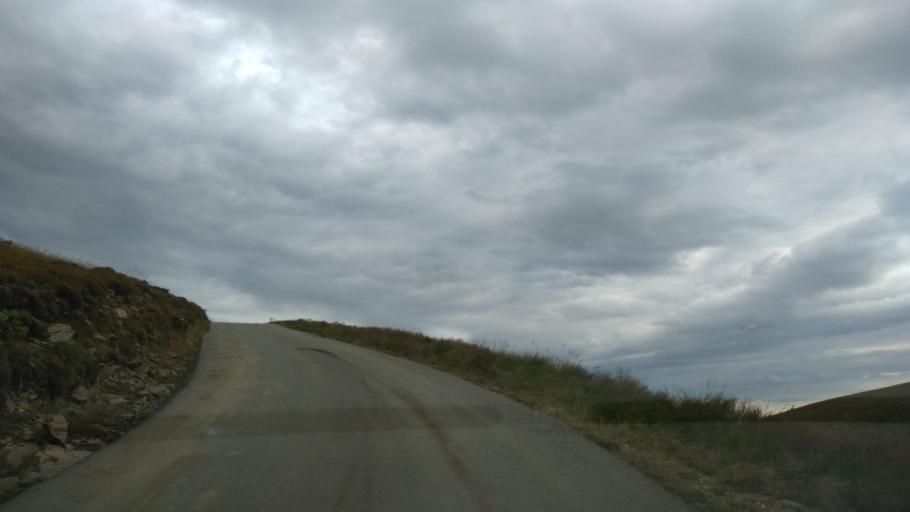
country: RO
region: Hunedoara
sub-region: Municipiul  Vulcan
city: Jiu-Paroseni
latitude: 45.3131
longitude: 23.3060
